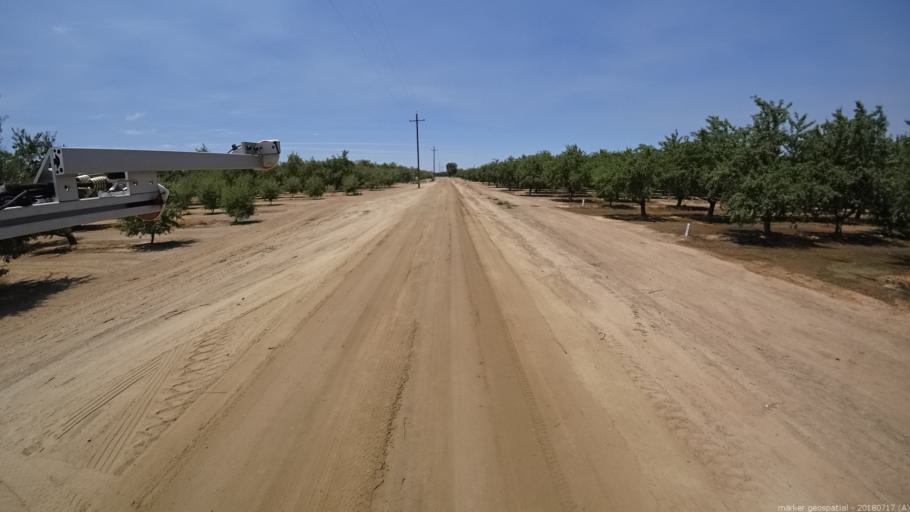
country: US
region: California
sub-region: Madera County
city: Fairmead
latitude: 37.1196
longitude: -120.1414
